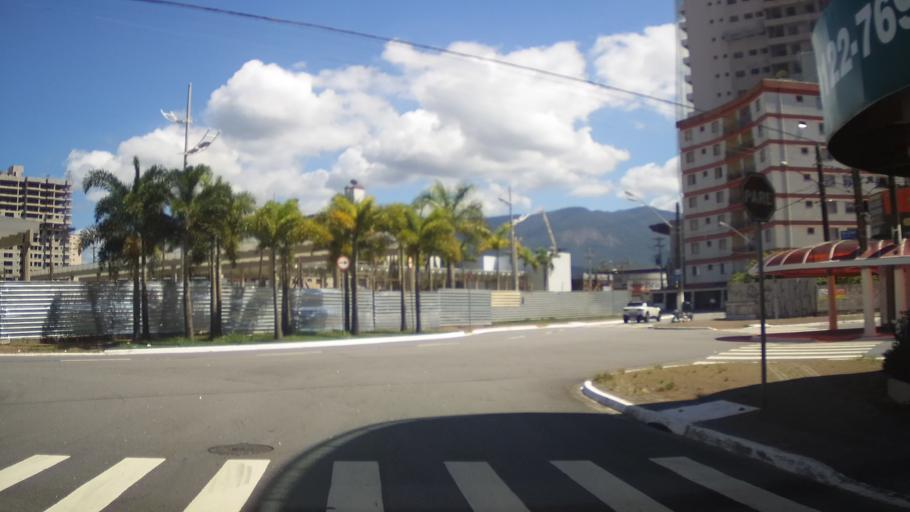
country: BR
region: Sao Paulo
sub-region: Mongagua
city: Mongagua
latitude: -24.0490
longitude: -46.5278
